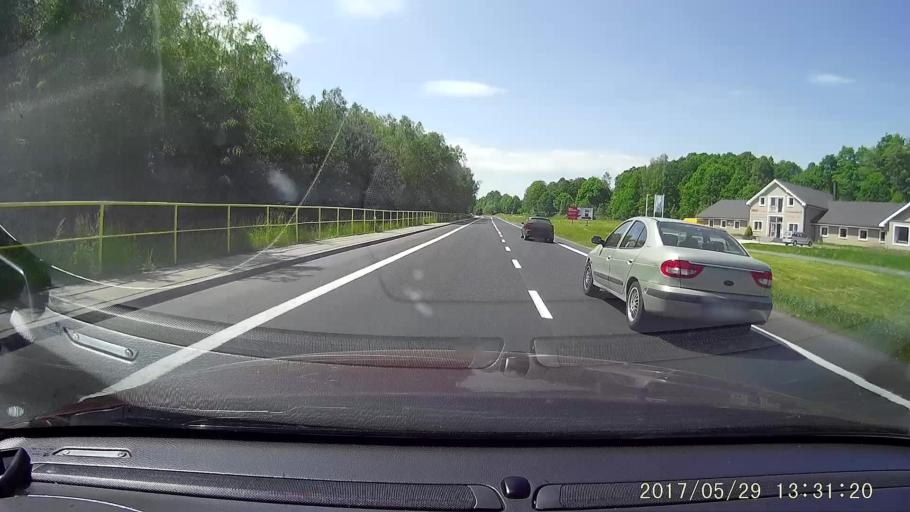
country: PL
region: Lower Silesian Voivodeship
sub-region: Powiat lubanski
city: Olszyna
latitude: 51.0790
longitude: 15.3452
